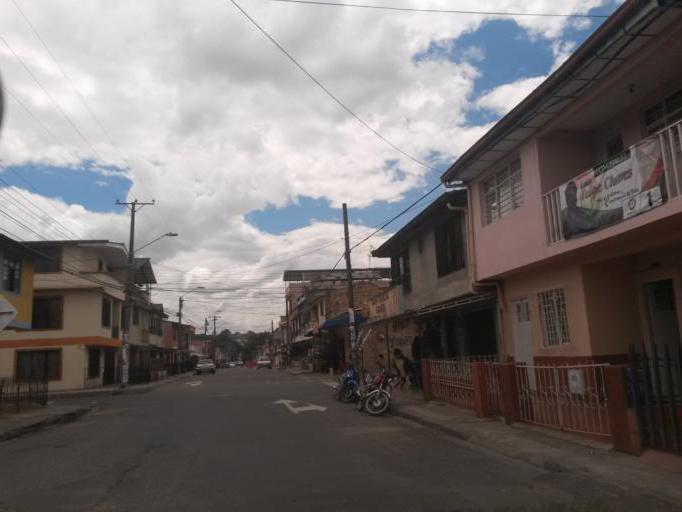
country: CO
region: Cauca
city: Popayan
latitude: 2.4477
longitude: -76.6237
